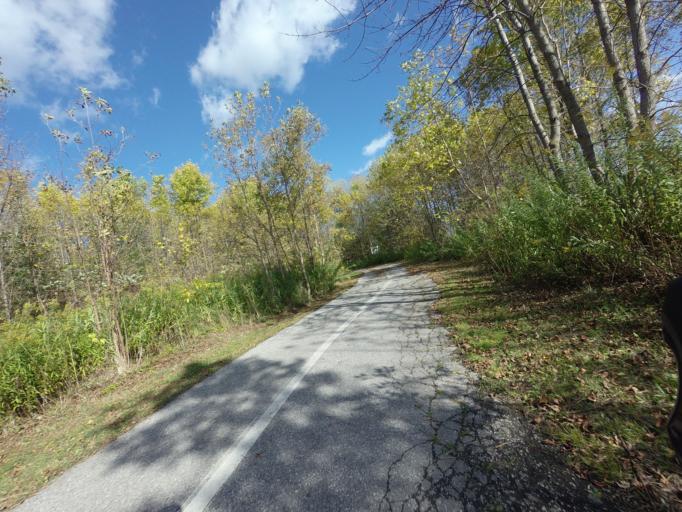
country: CA
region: Ontario
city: Ajax
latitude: 43.8307
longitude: -78.9757
